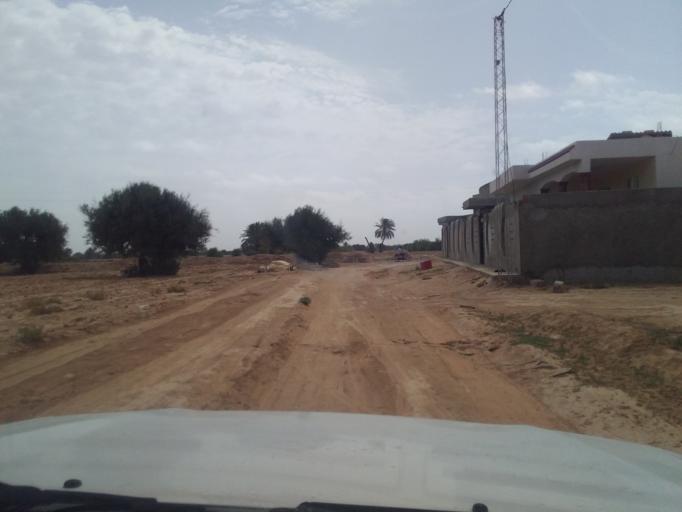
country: TN
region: Qabis
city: Matmata
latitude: 33.6191
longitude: 10.2673
